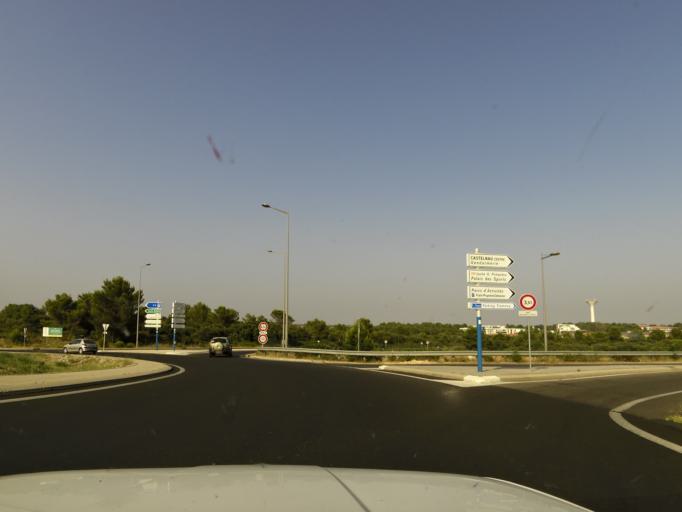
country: FR
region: Languedoc-Roussillon
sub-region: Departement de l'Herault
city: Jacou
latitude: 43.6515
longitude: 3.9211
